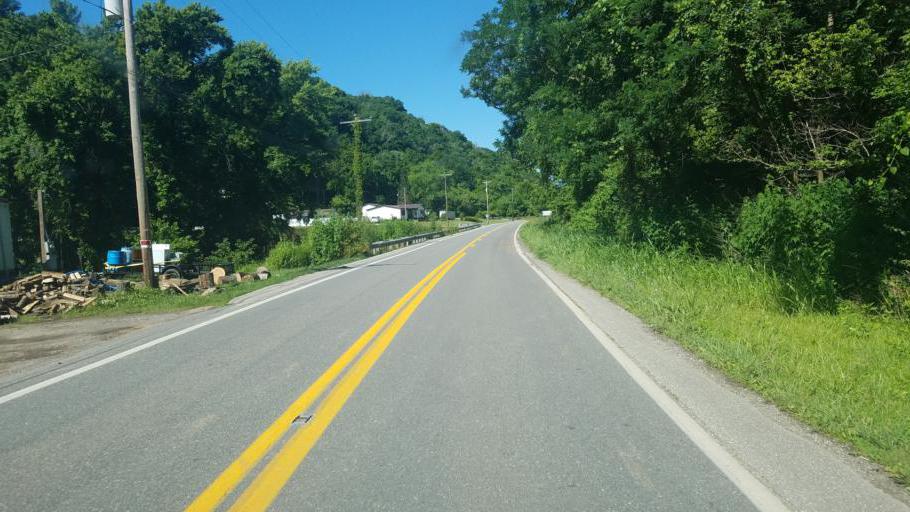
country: US
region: West Virginia
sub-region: Cabell County
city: Lesage
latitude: 38.5917
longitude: -82.1869
